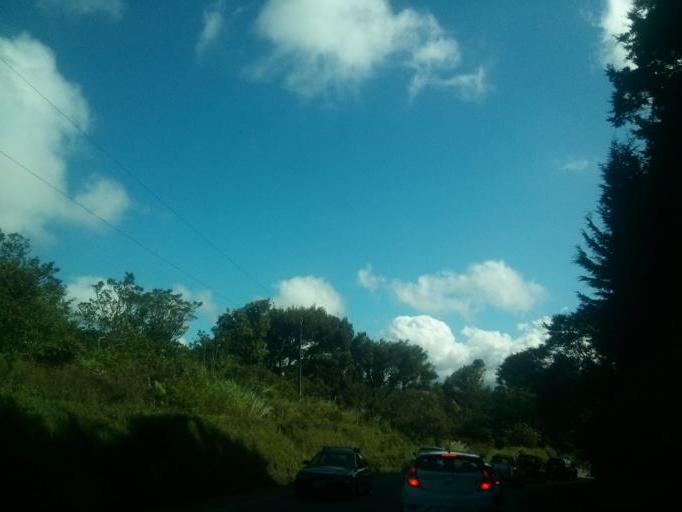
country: CR
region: Cartago
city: Cot
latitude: 9.8861
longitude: -83.8848
